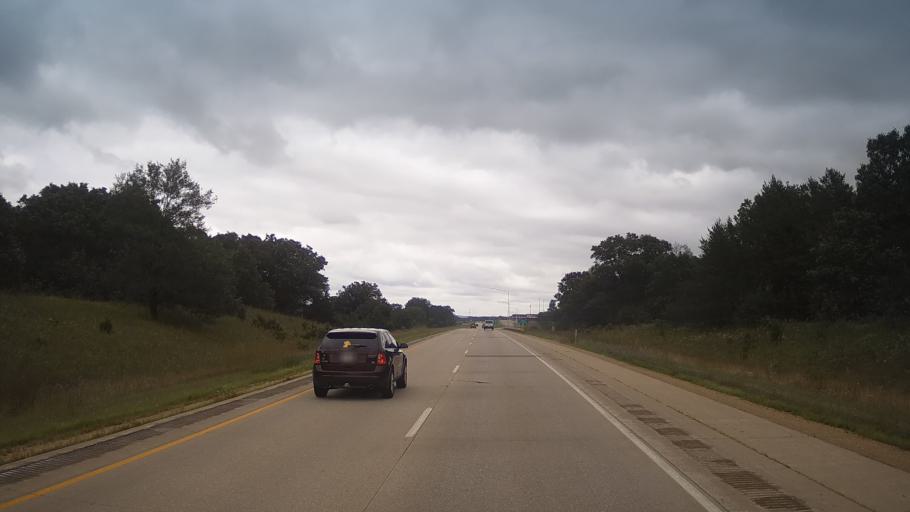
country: US
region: Wisconsin
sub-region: Monroe County
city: Sparta
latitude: 43.9079
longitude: -90.8806
